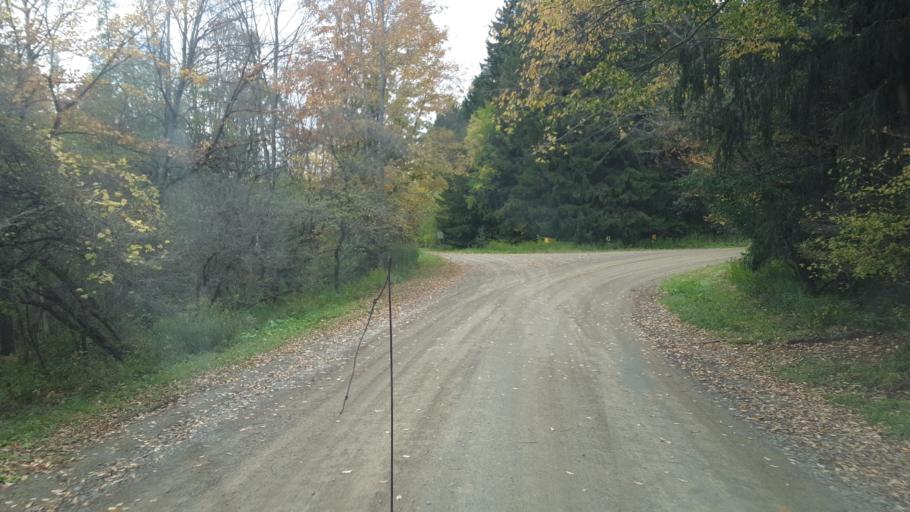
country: US
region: New York
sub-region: Allegany County
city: Alfred
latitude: 42.3693
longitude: -77.8478
